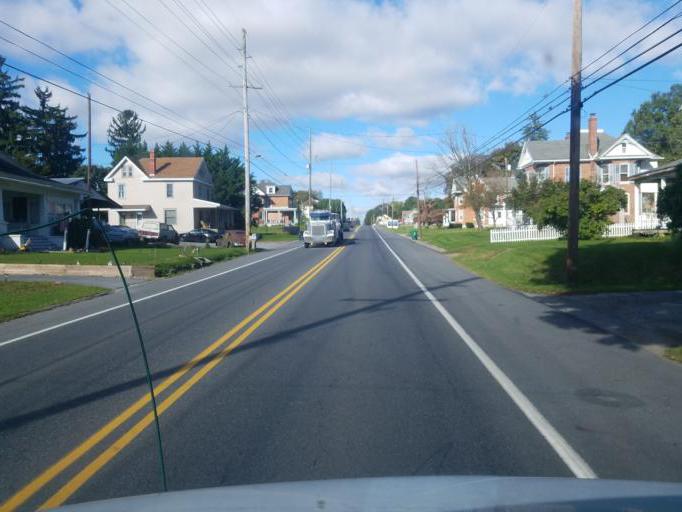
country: US
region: Pennsylvania
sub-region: Franklin County
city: Waynesboro
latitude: 39.7693
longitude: -77.6270
